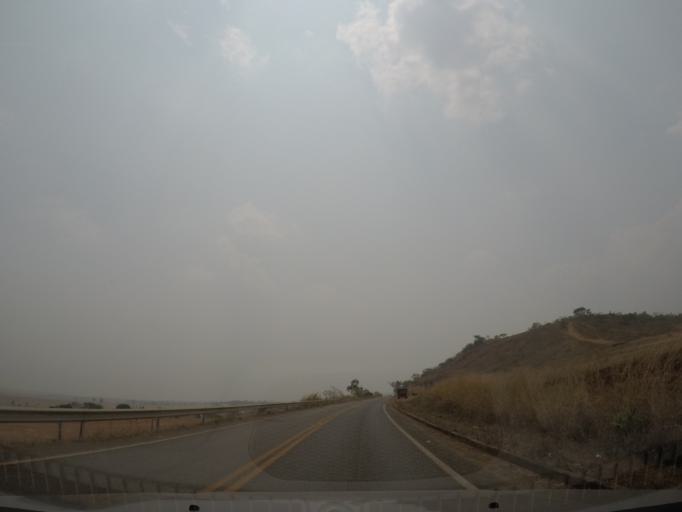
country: BR
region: Goias
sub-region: Pirenopolis
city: Pirenopolis
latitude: -15.9281
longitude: -48.8507
